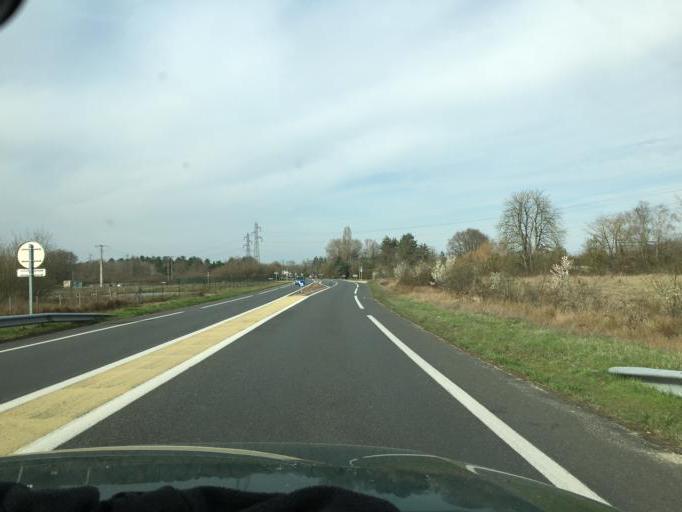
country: FR
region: Centre
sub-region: Departement du Loiret
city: La Ferte-Saint-Aubin
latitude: 47.7696
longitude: 1.9370
